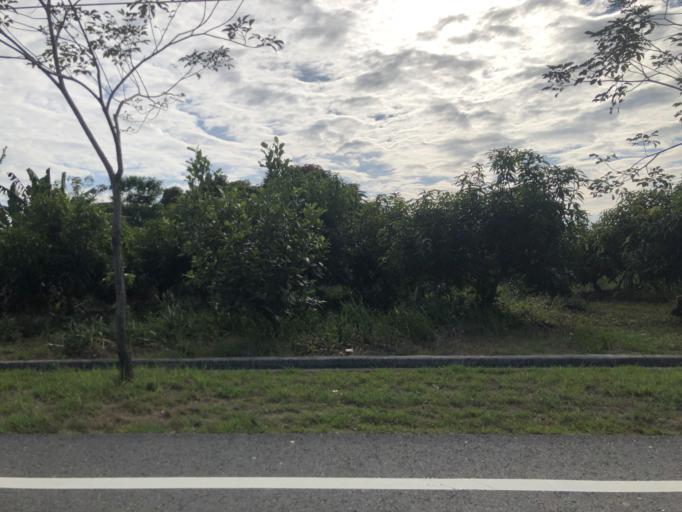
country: TW
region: Taiwan
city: Yujing
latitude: 23.0529
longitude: 120.4163
